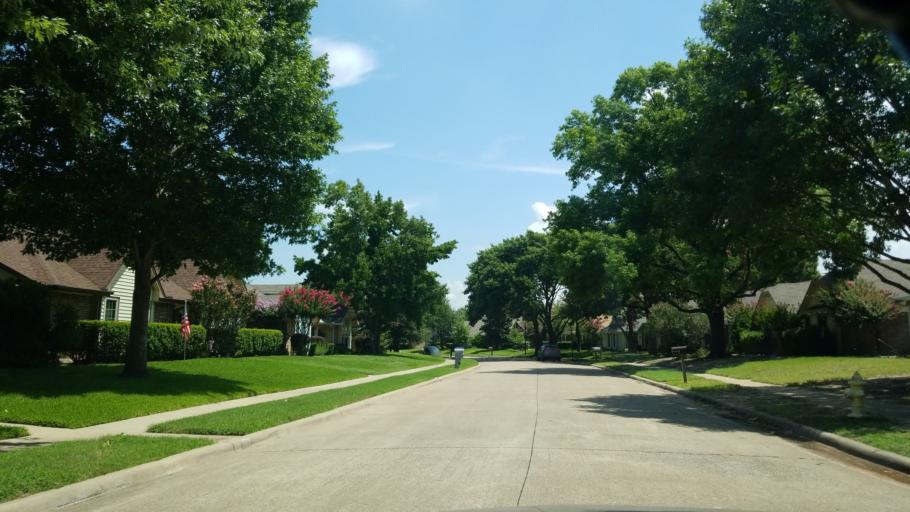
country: US
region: Texas
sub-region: Dallas County
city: Coppell
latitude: 32.9652
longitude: -96.9674
